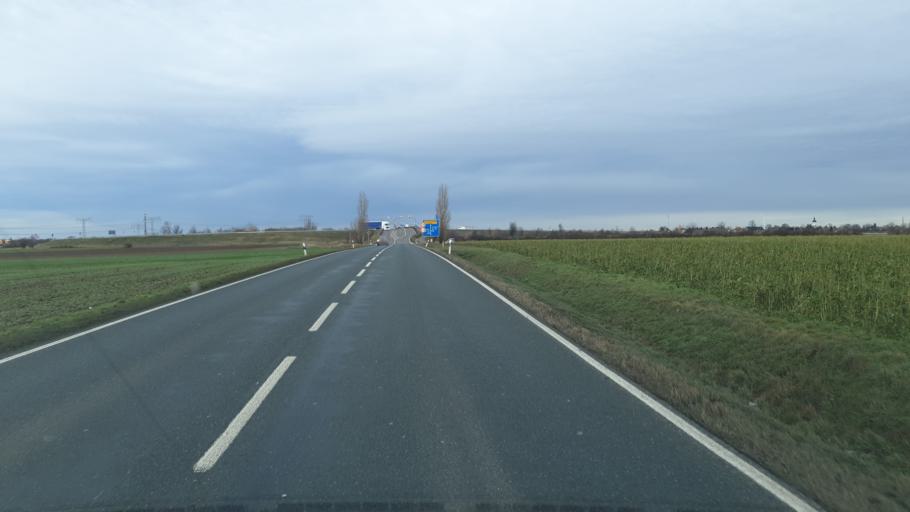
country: DE
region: Saxony
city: Kitzen
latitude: 51.2594
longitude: 12.2705
